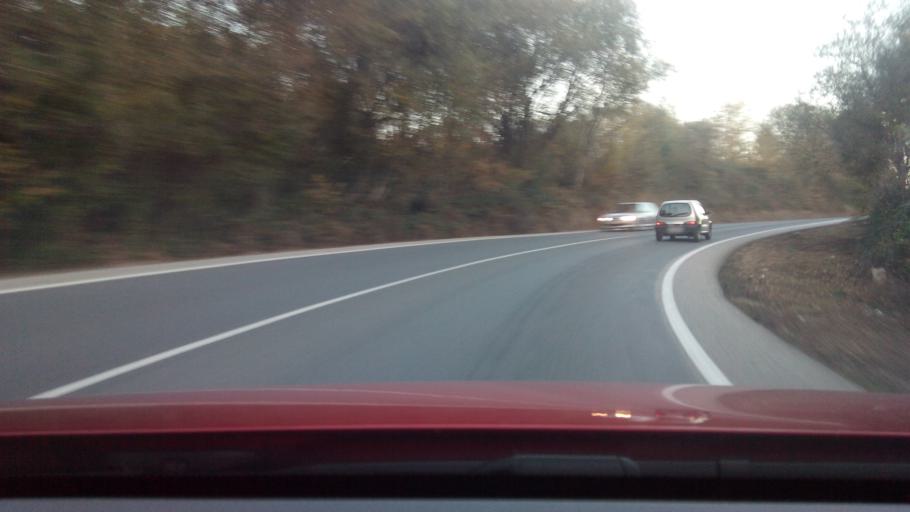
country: ES
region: Galicia
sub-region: Provincia de Pontevedra
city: Gondomar
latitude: 42.1605
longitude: -8.7016
